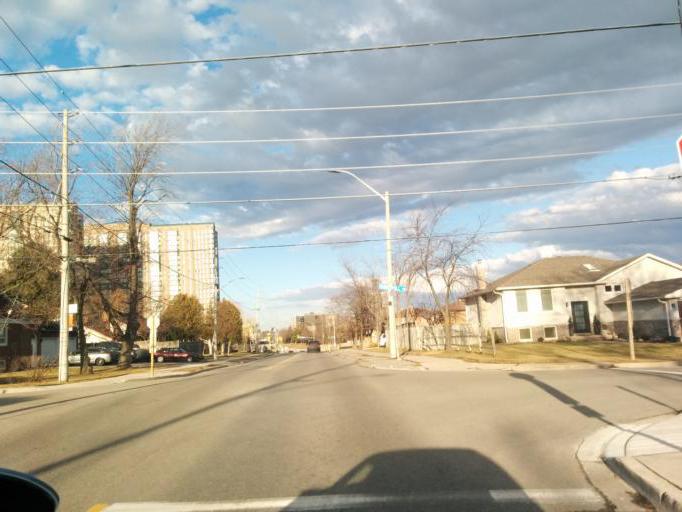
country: CA
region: Ontario
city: Mississauga
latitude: 43.5776
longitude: -79.6260
